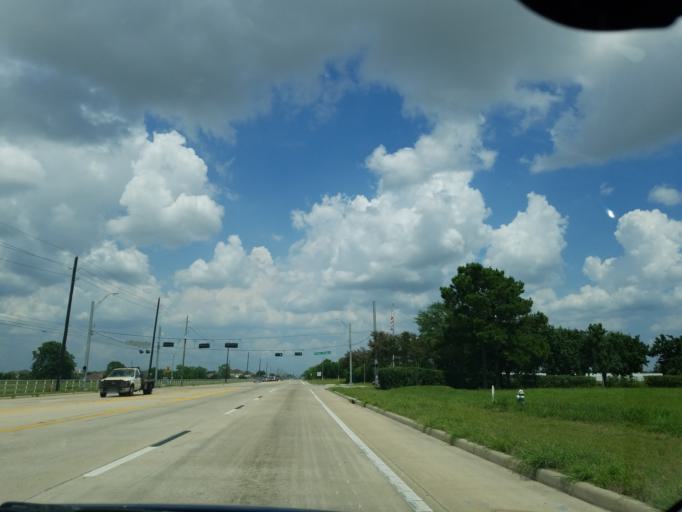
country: US
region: Texas
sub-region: Harris County
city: Cypress
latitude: 29.8796
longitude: -95.7328
